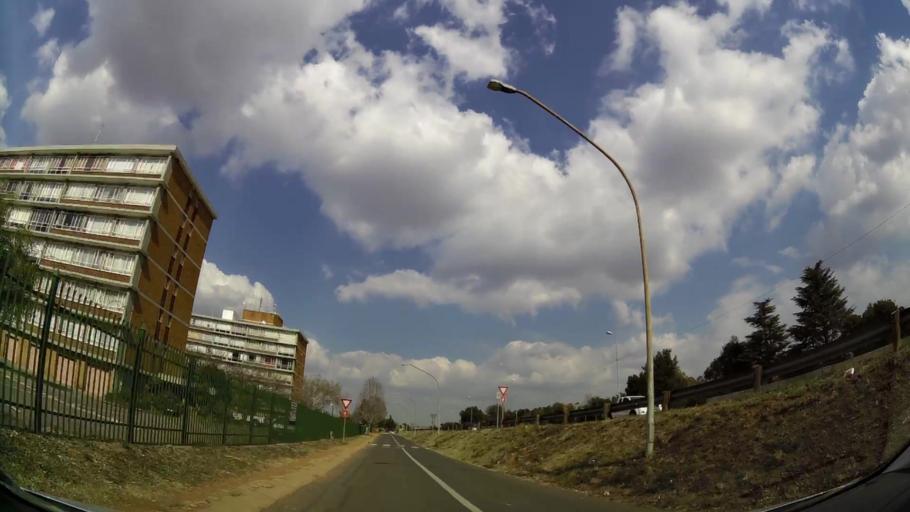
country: ZA
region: Gauteng
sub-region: City of Tshwane Metropolitan Municipality
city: Centurion
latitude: -25.8247
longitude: 28.2558
